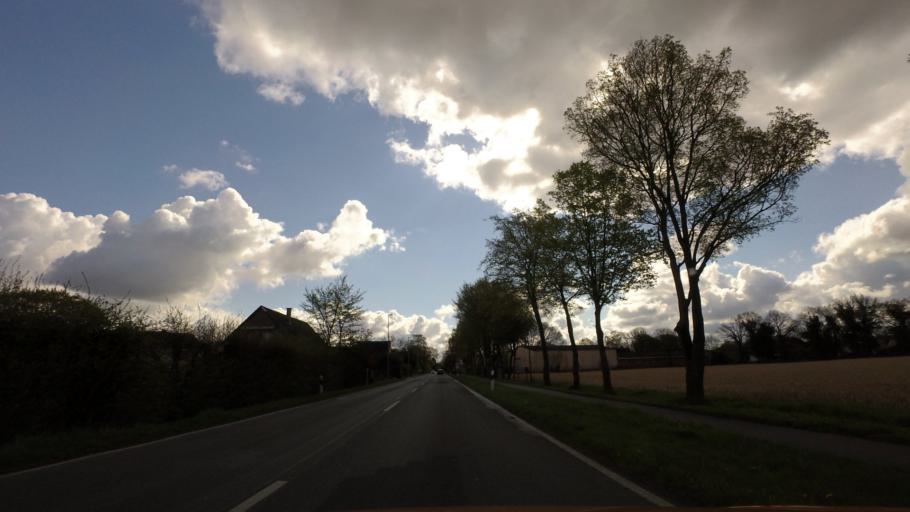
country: DE
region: Lower Saxony
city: Ganderkesee
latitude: 53.0494
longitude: 8.4829
